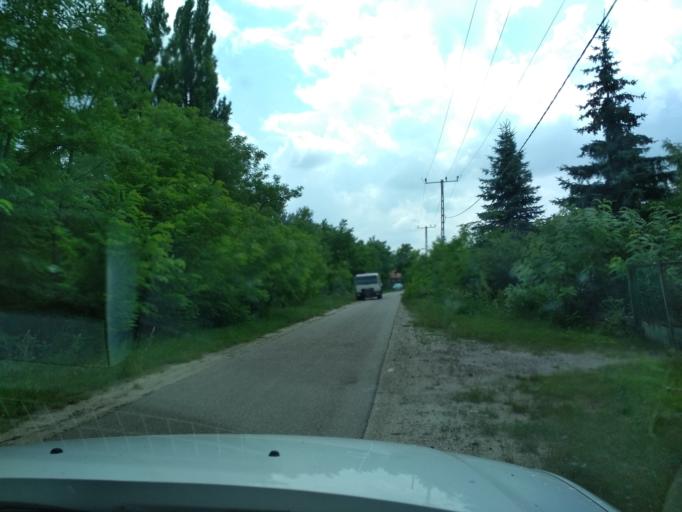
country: HU
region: Pest
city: Tapioszentmarton
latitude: 47.3742
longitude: 19.7561
